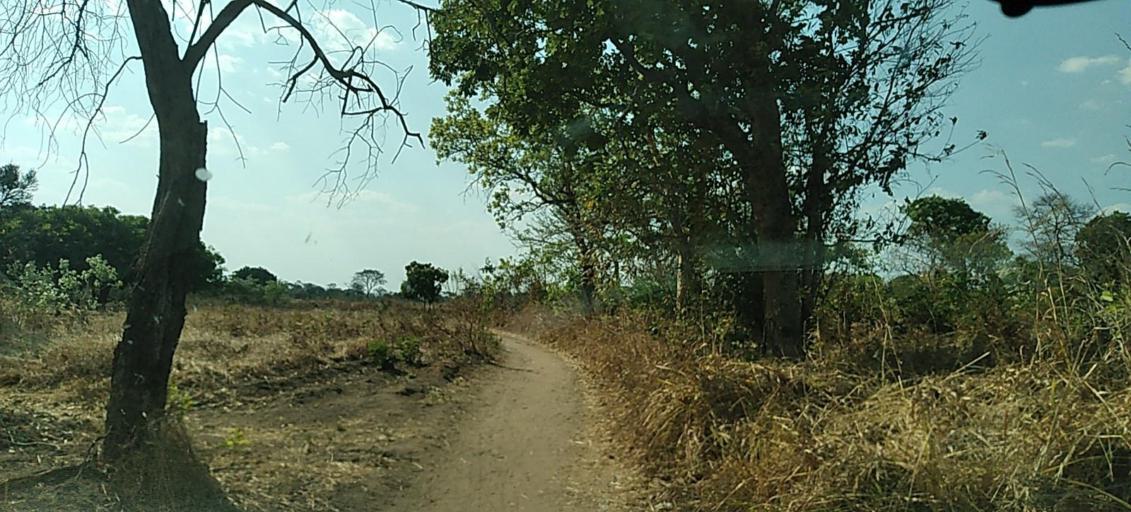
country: ZM
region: North-Western
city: Kalengwa
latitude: -13.0564
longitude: 24.9546
